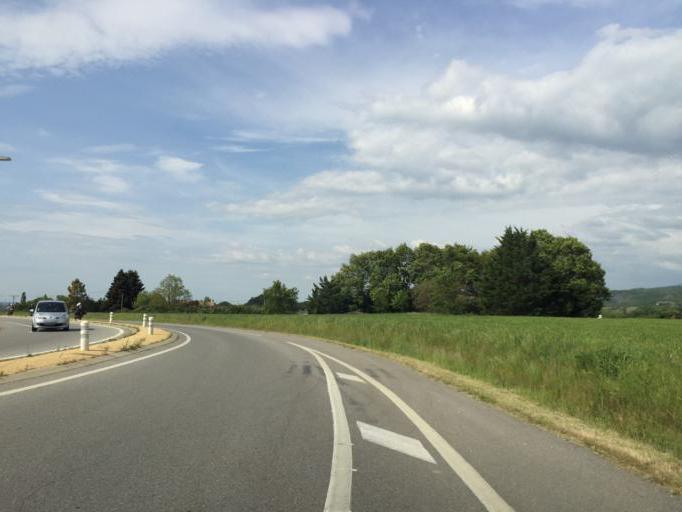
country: FR
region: Rhone-Alpes
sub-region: Departement de la Drome
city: Upie
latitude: 44.8196
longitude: 5.0110
